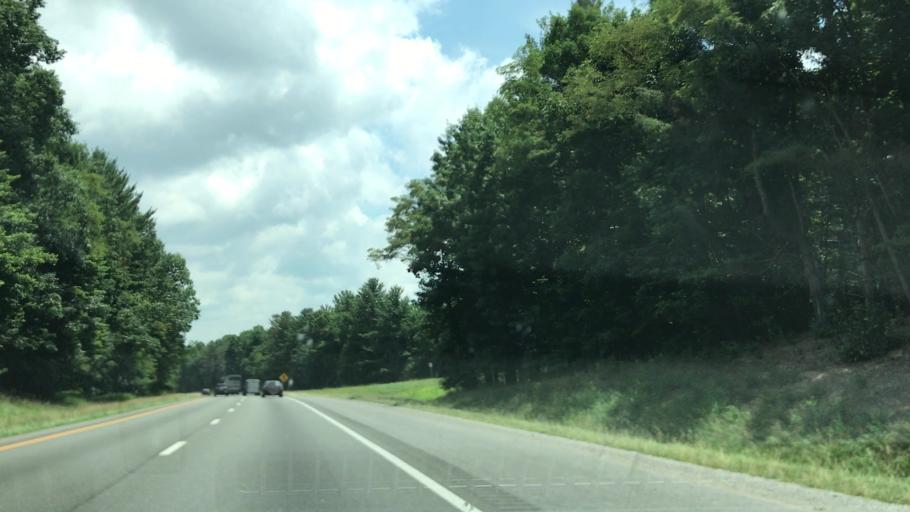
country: US
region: Virginia
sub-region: Carroll County
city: Woodlawn
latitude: 36.7820
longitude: -80.8295
